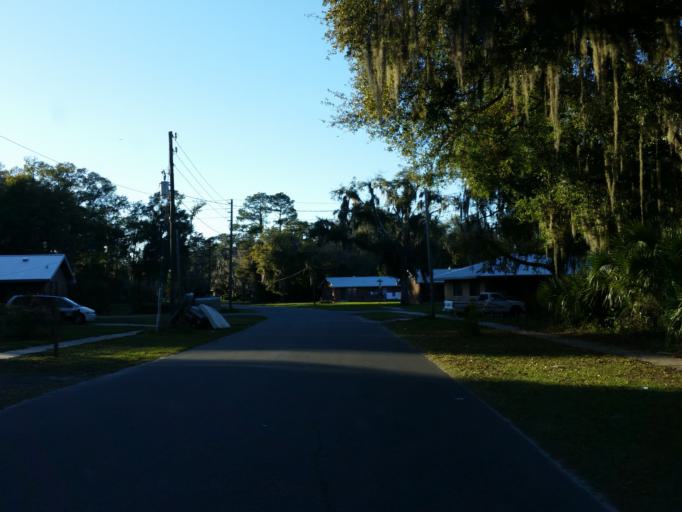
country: US
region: Florida
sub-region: Hamilton County
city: Jasper
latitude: 30.5207
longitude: -82.9474
